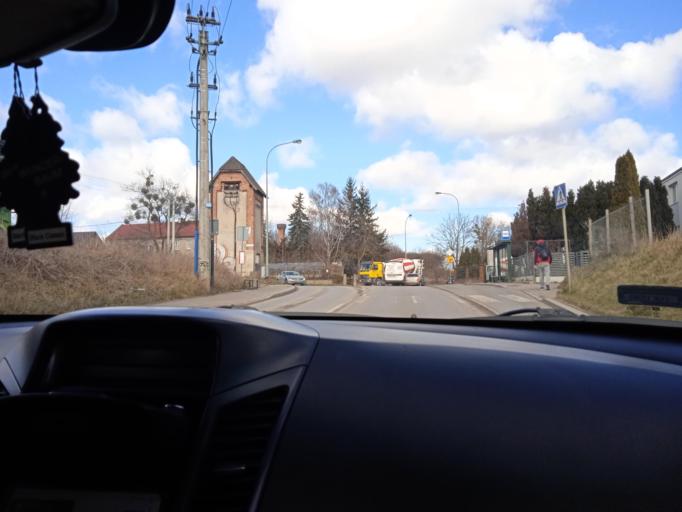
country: PL
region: Pomeranian Voivodeship
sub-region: Powiat gdanski
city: Kowale
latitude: 54.3280
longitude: 18.5517
